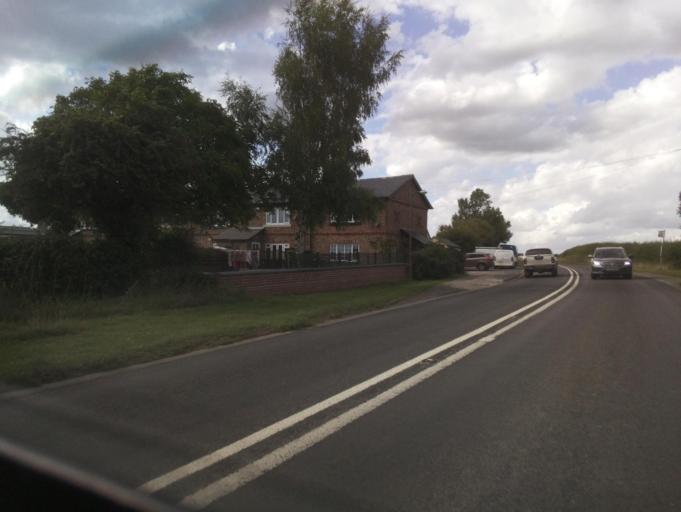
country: GB
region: England
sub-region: North Yorkshire
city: Ripon
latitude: 54.1606
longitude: -1.5423
